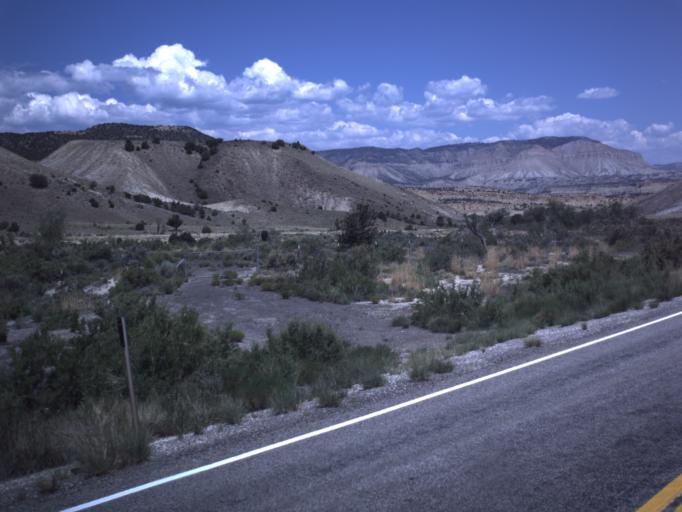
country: US
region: Utah
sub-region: Emery County
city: Ferron
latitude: 38.7700
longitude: -111.3480
